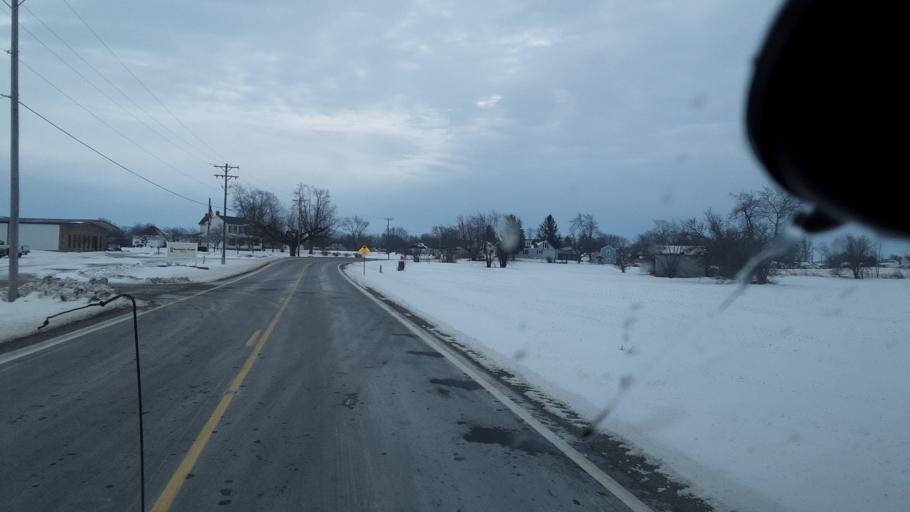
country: US
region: Ohio
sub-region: Madison County
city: Bethel
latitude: 39.7387
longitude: -83.4773
